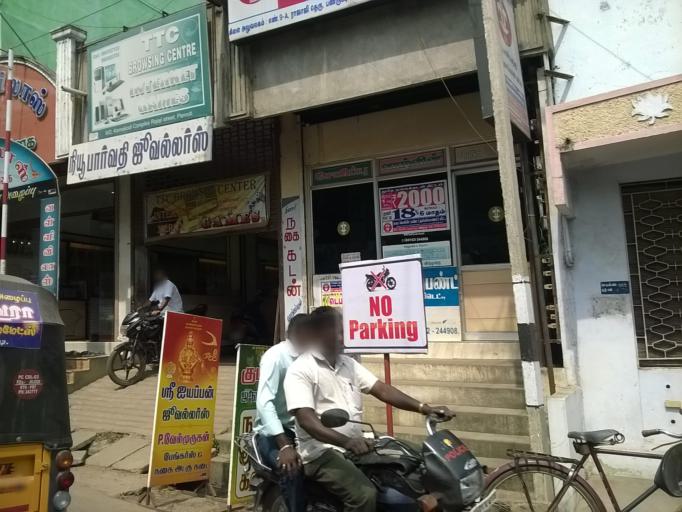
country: IN
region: Tamil Nadu
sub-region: Cuddalore
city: Panruti
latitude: 11.7735
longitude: 79.5497
